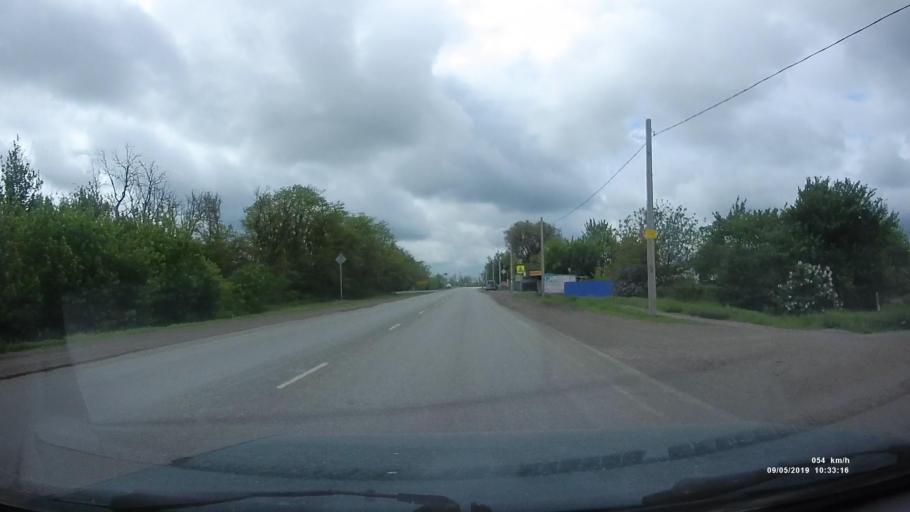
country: RU
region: Rostov
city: Azov
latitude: 47.0649
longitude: 39.4250
